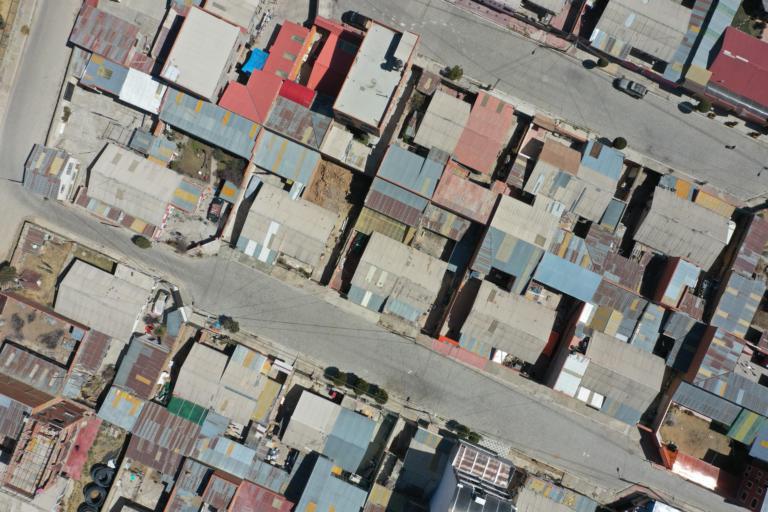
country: BO
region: La Paz
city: La Paz
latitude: -16.5321
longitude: -68.1560
